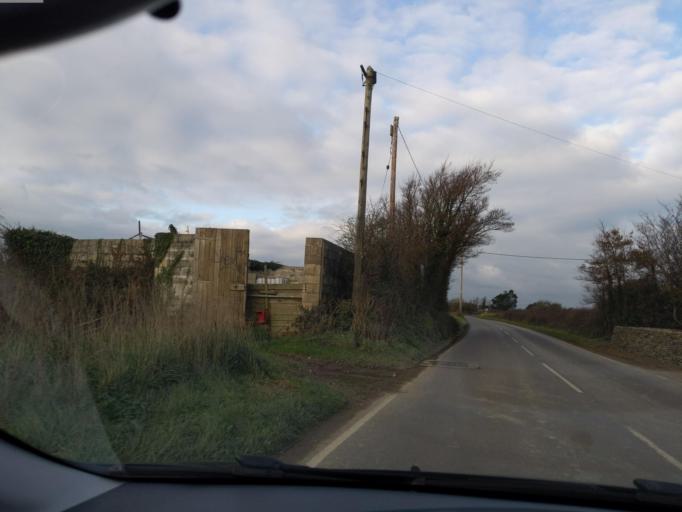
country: GB
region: England
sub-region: Cornwall
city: Padstow
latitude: 50.5220
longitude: -4.9518
